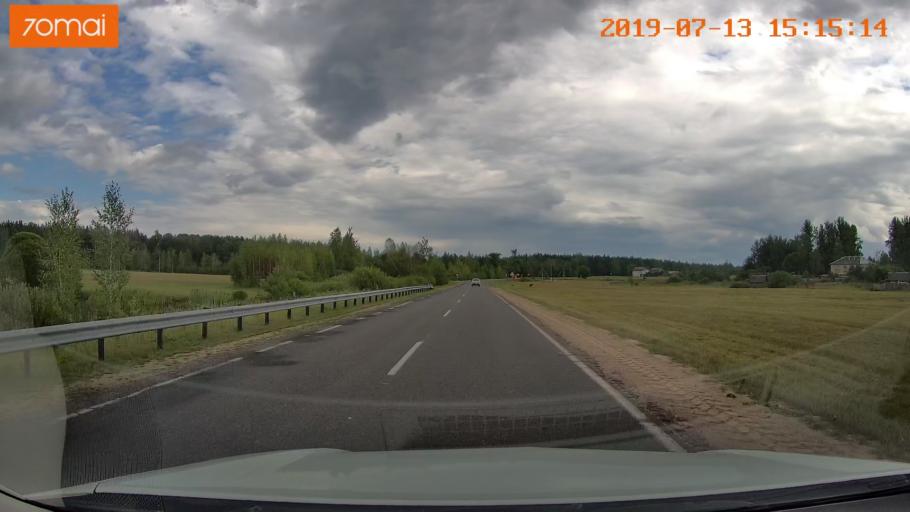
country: BY
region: Mogilev
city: Hlusha
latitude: 53.1184
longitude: 28.8239
